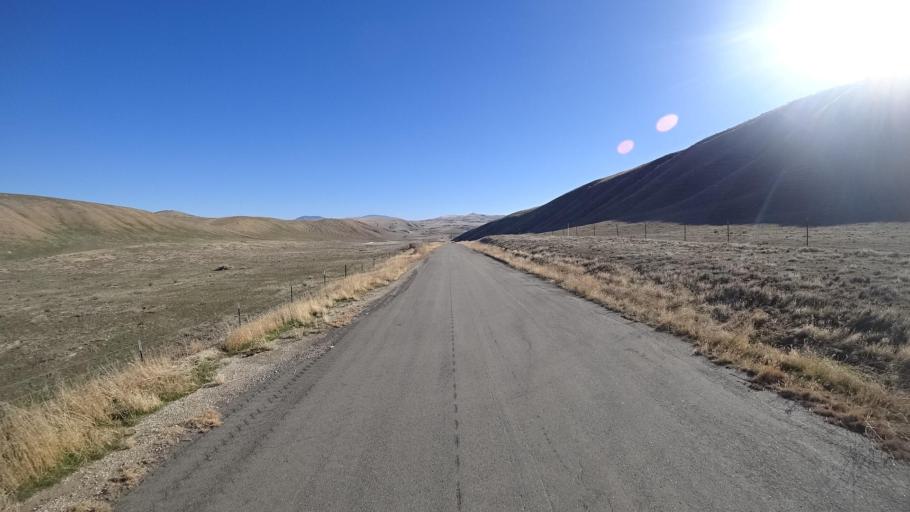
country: US
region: California
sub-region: Kern County
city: Maricopa
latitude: 34.9782
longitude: -119.4647
